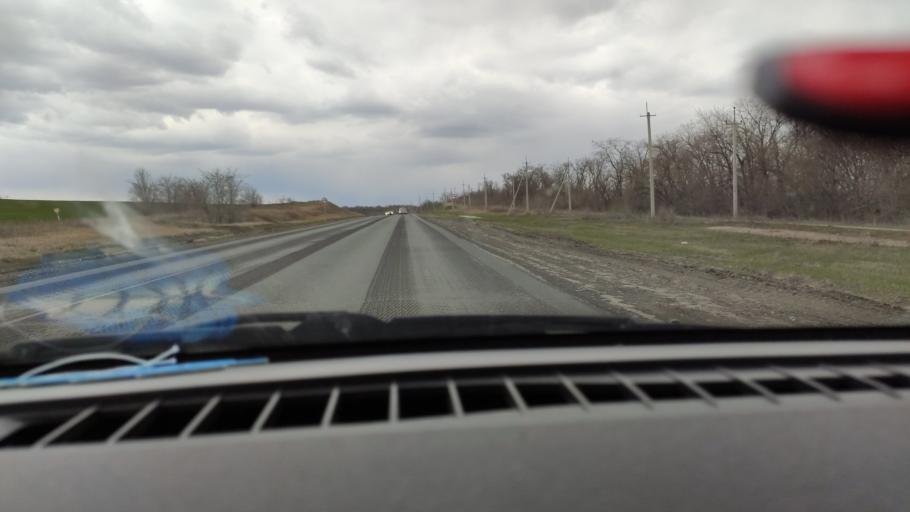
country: RU
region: Saratov
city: Shumeyka
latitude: 51.7848
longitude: 46.1344
